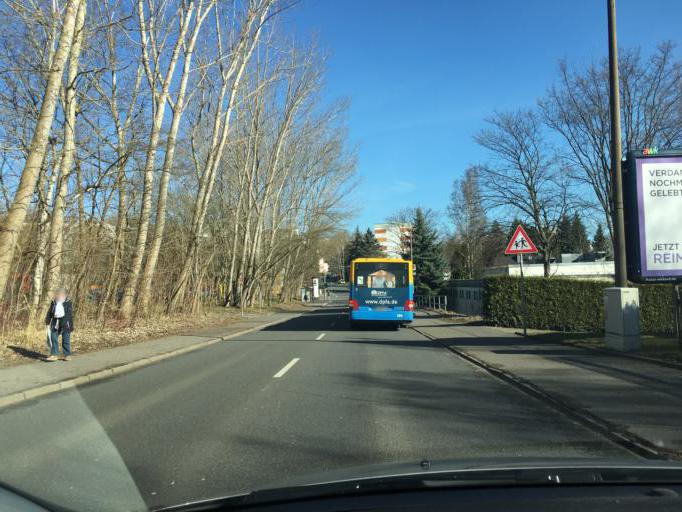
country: DE
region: Saxony
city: Neukirchen
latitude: 50.8040
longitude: 12.8980
